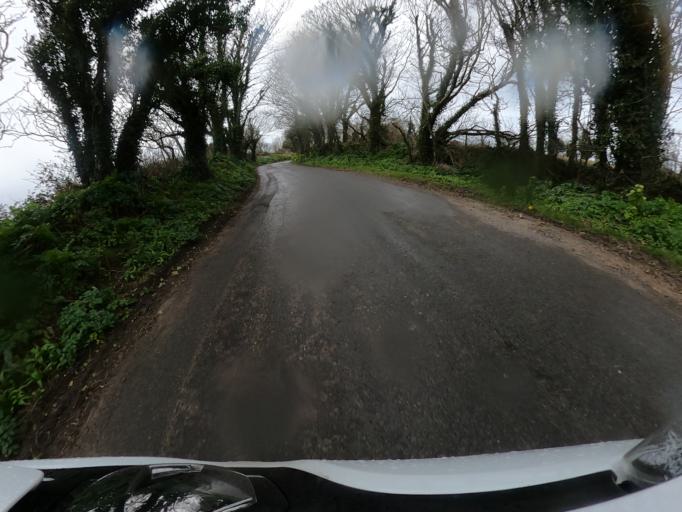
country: IM
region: Ramsey
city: Ramsey
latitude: 54.3825
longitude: -4.4647
